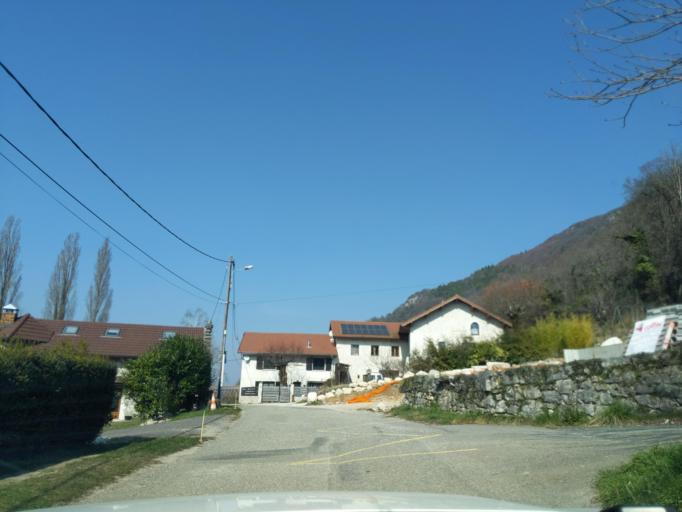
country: FR
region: Rhone-Alpes
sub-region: Departement de la Haute-Savoie
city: Moye
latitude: 45.9109
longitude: 5.8492
